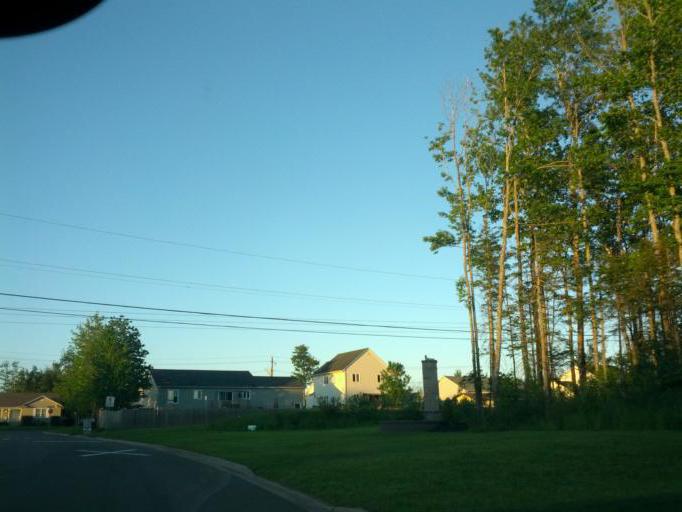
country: CA
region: New Brunswick
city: Moncton
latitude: 46.1133
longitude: -64.8678
